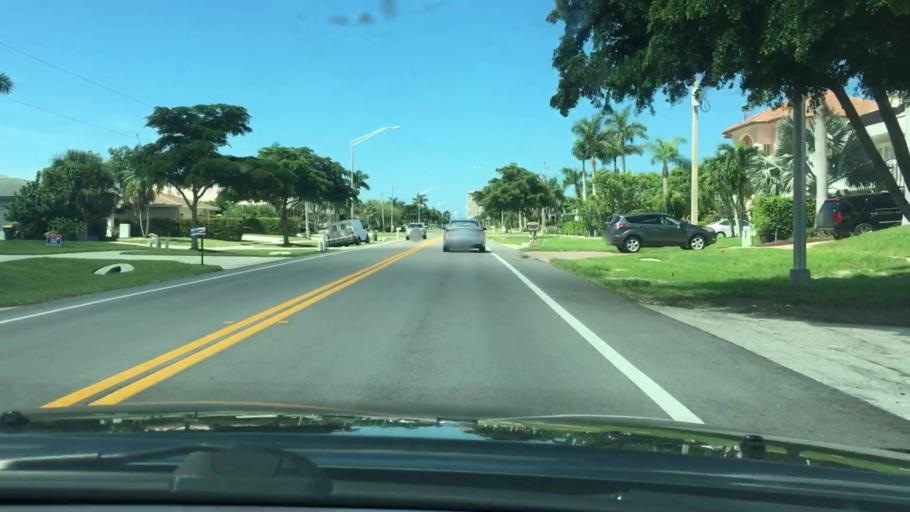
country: US
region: Florida
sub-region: Collier County
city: Marco
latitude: 25.9371
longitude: -81.7183
